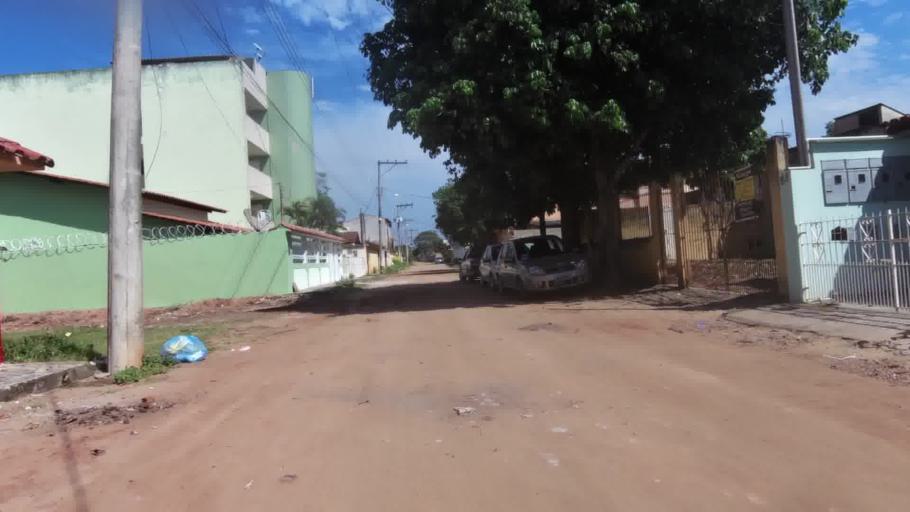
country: BR
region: Espirito Santo
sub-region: Piuma
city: Piuma
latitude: -20.8418
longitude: -40.7372
